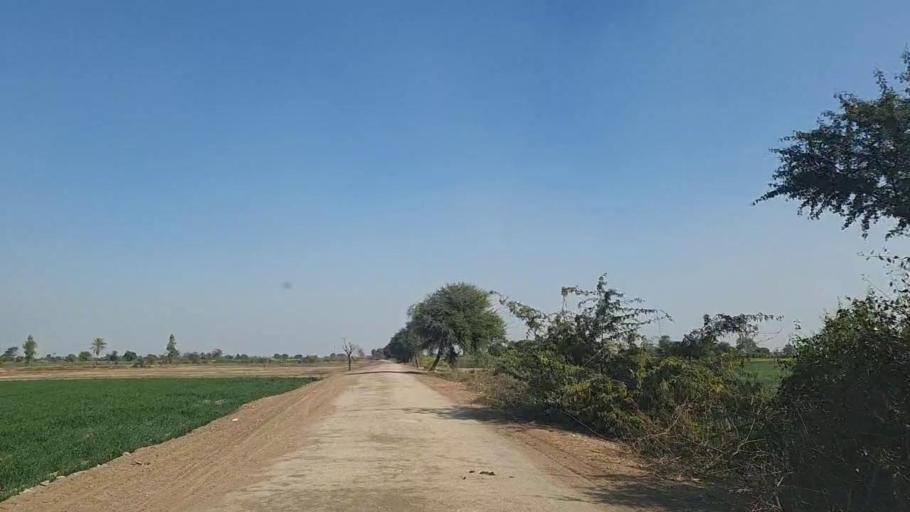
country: PK
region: Sindh
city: Shahpur Chakar
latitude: 26.2092
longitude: 68.6216
